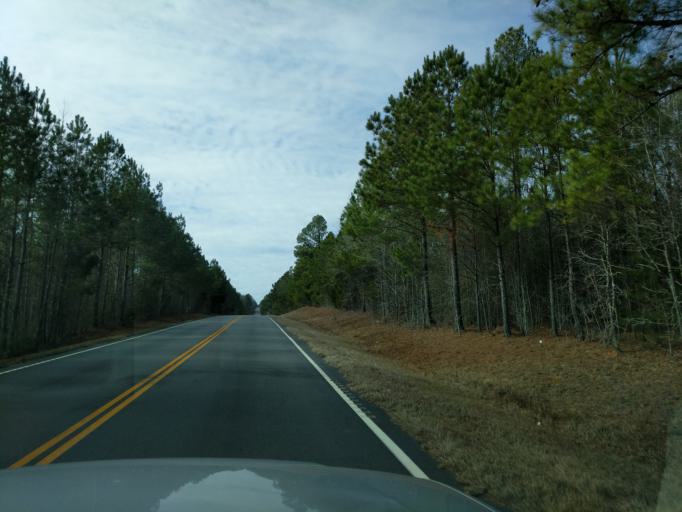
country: US
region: South Carolina
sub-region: Edgefield County
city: Edgefield
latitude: 33.9338
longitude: -81.9739
